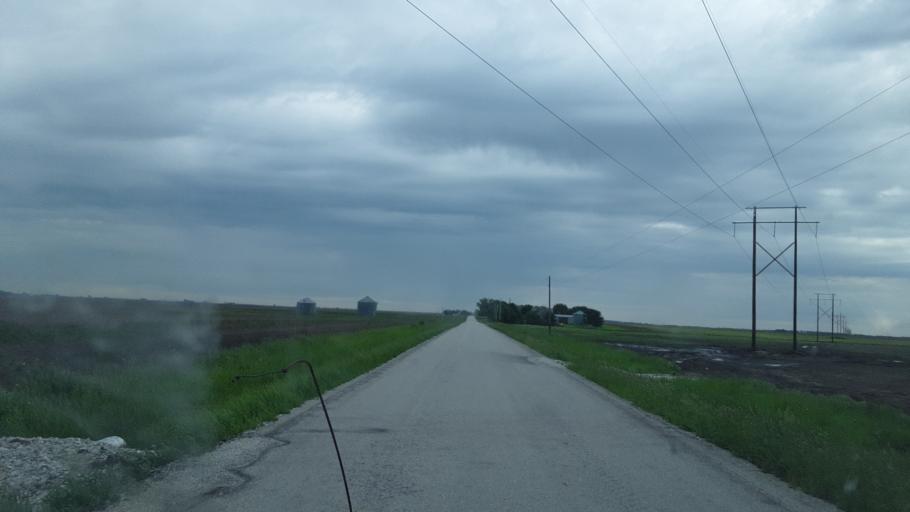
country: US
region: Illinois
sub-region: McDonough County
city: Macomb
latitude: 40.3811
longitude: -90.5231
